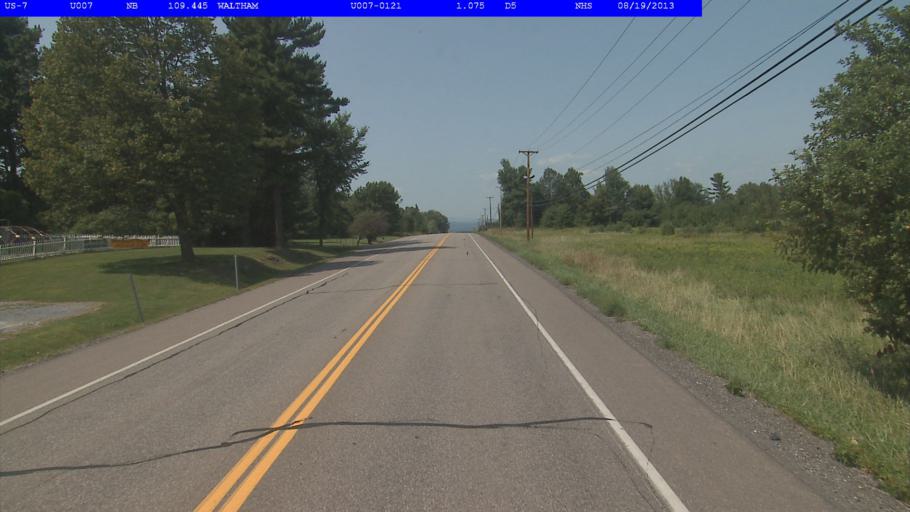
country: US
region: Vermont
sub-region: Addison County
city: Vergennes
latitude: 44.1585
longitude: -73.2255
